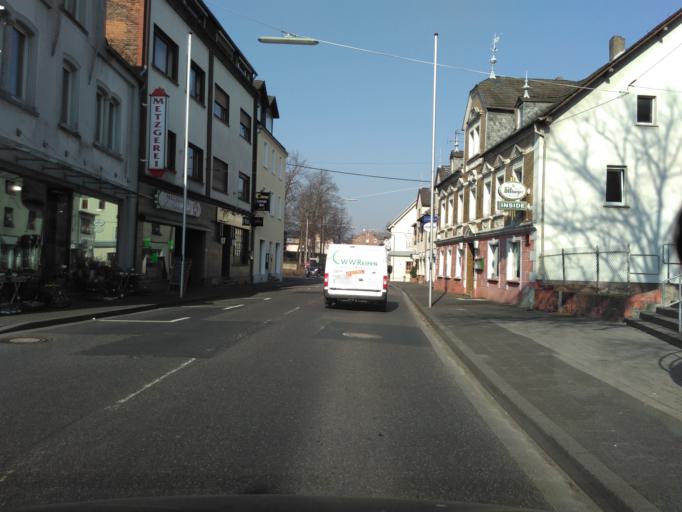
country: DE
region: Rheinland-Pfalz
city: Wirges
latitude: 50.4728
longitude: 7.8007
